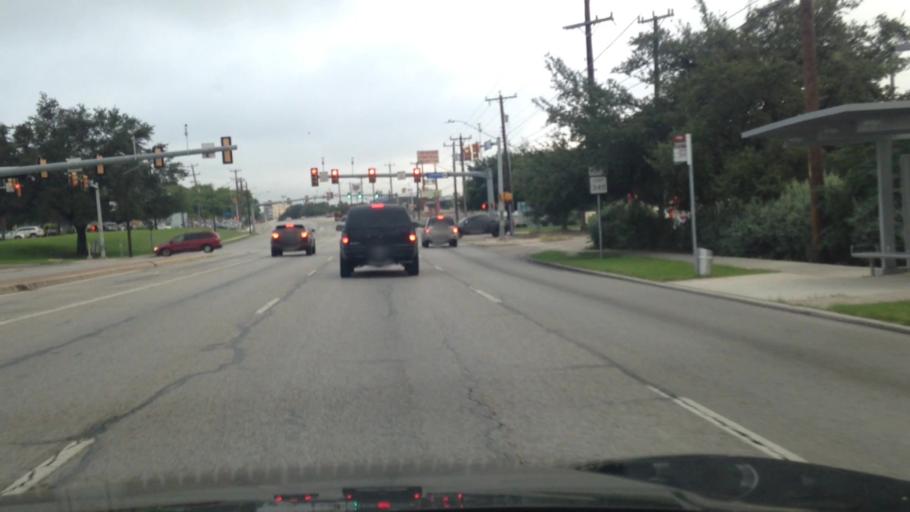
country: US
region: Texas
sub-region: Bexar County
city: Balcones Heights
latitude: 29.4955
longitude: -98.5553
